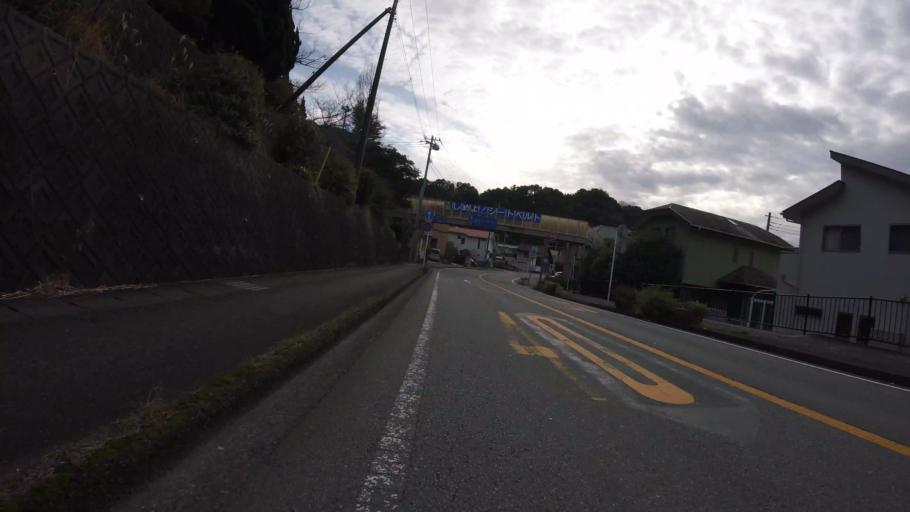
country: JP
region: Shizuoka
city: Numazu
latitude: 35.0828
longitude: 138.8833
